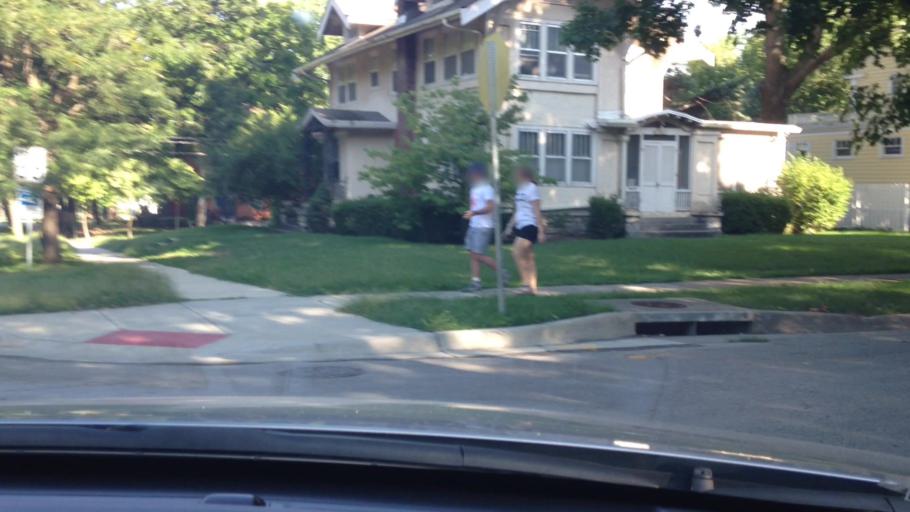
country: US
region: Kansas
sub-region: Johnson County
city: Mission Hills
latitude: 39.0277
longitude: -94.5914
